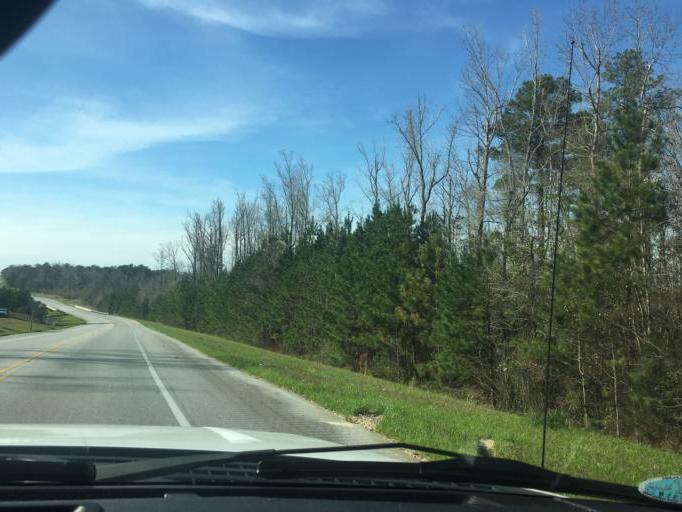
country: US
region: Alabama
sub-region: Lee County
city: Auburn
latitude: 32.4307
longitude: -85.4644
